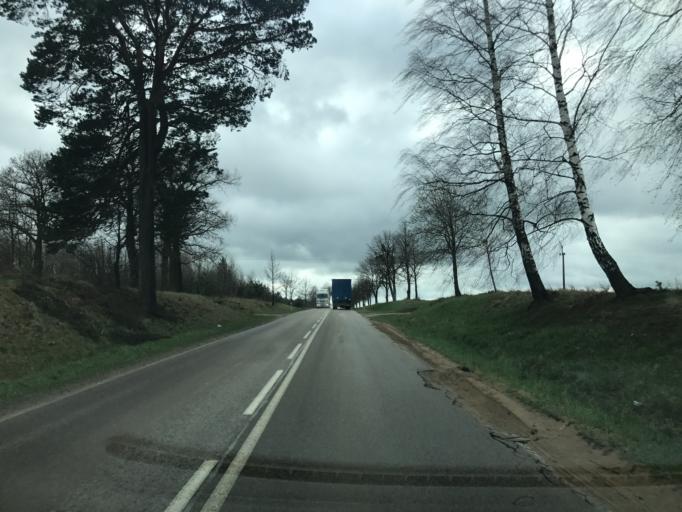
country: PL
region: Warmian-Masurian Voivodeship
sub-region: Powiat olsztynski
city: Olsztynek
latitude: 53.5159
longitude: 20.2061
